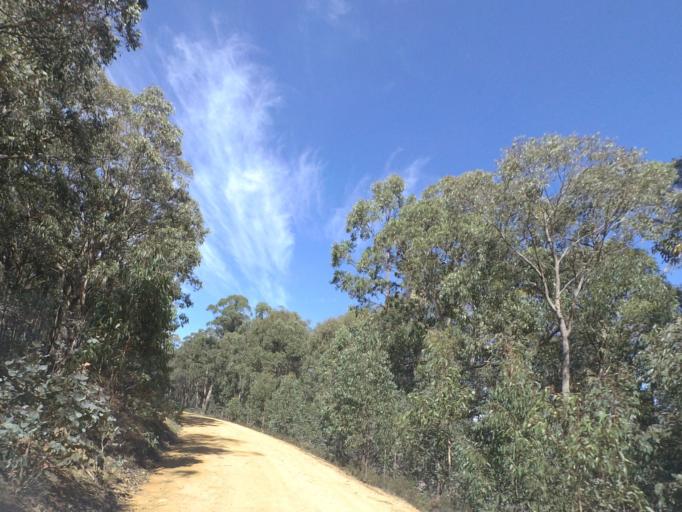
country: AU
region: Victoria
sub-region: Moorabool
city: Bacchus Marsh
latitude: -37.4371
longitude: 144.3622
